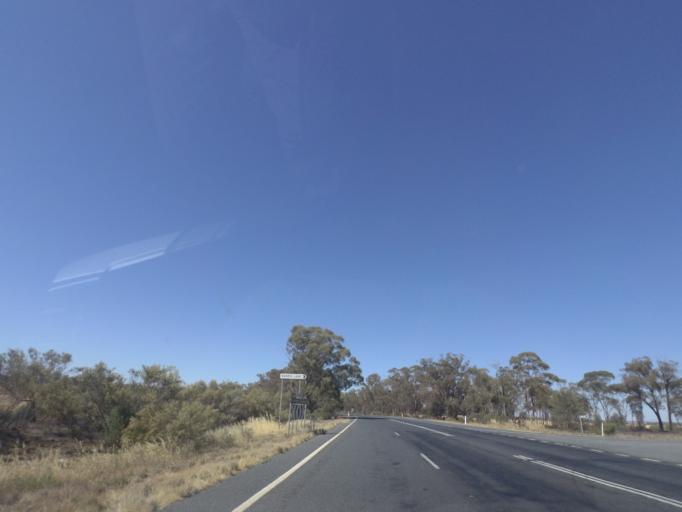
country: AU
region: New South Wales
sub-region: Bland
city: West Wyalong
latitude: -34.1184
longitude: 147.1292
